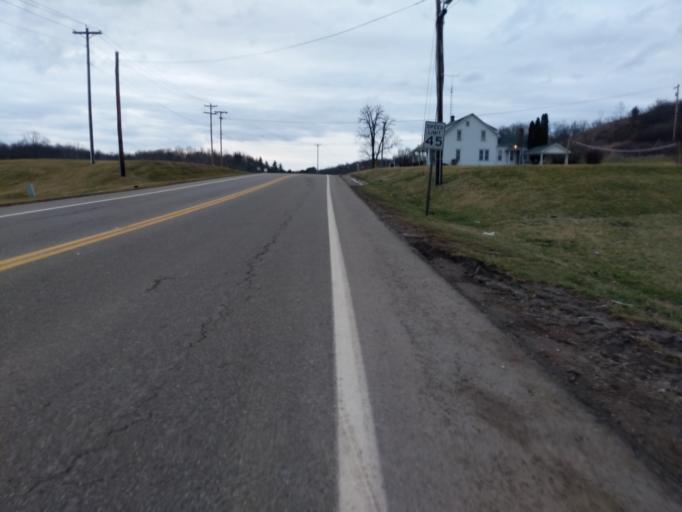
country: US
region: Ohio
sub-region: Athens County
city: Athens
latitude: 39.3320
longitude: -82.1301
